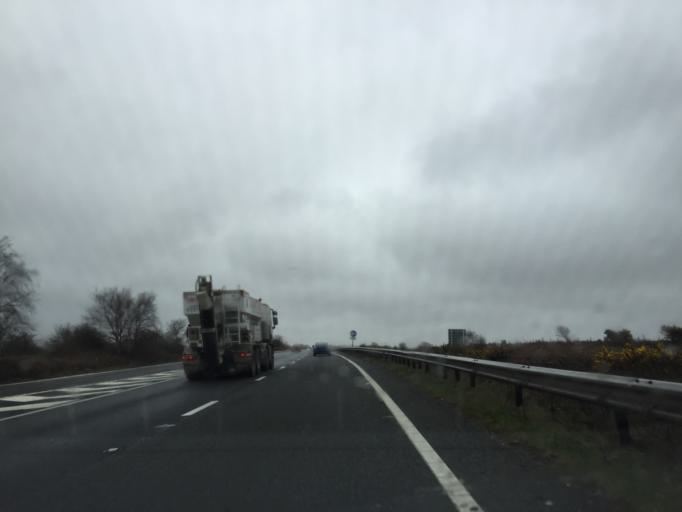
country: GB
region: England
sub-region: Hampshire
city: Ringwood
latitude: 50.8555
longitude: -1.7273
